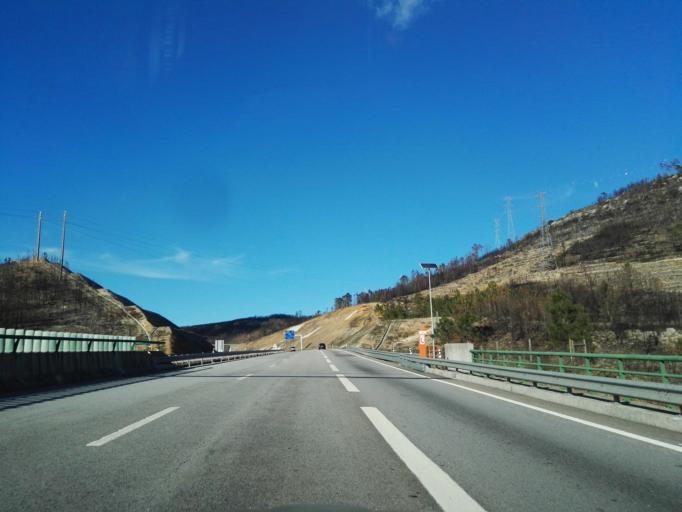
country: PT
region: Portalegre
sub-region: Nisa
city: Nisa
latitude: 39.6855
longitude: -7.7147
